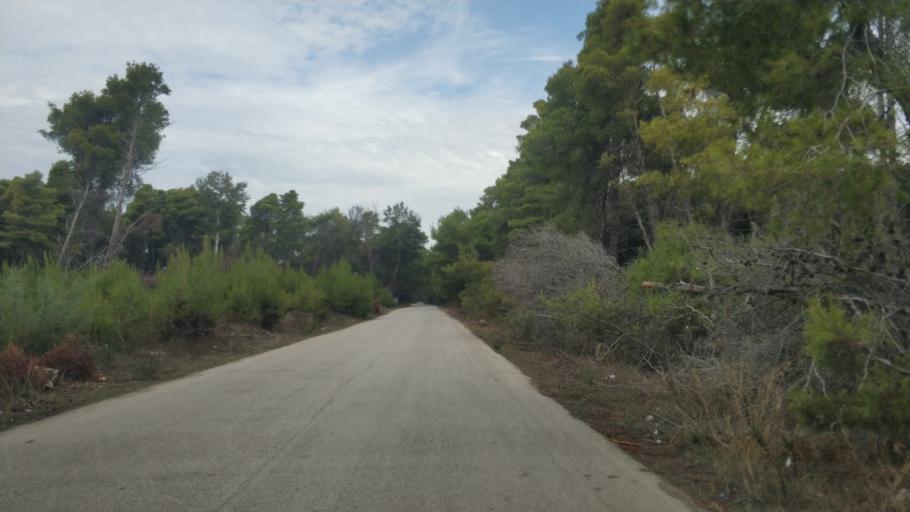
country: AL
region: Vlore
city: Vlore
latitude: 40.4811
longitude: 19.4493
